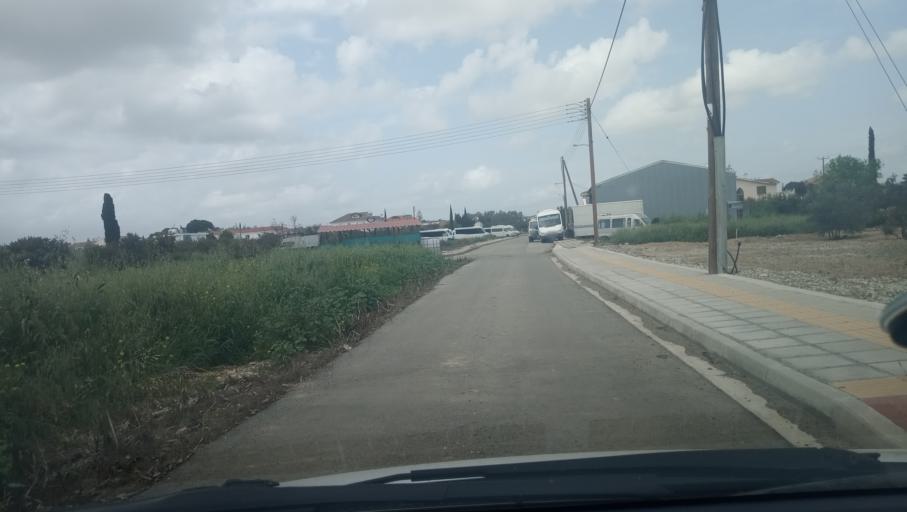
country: CY
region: Lefkosia
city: Pano Deftera
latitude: 35.0738
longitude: 33.2662
